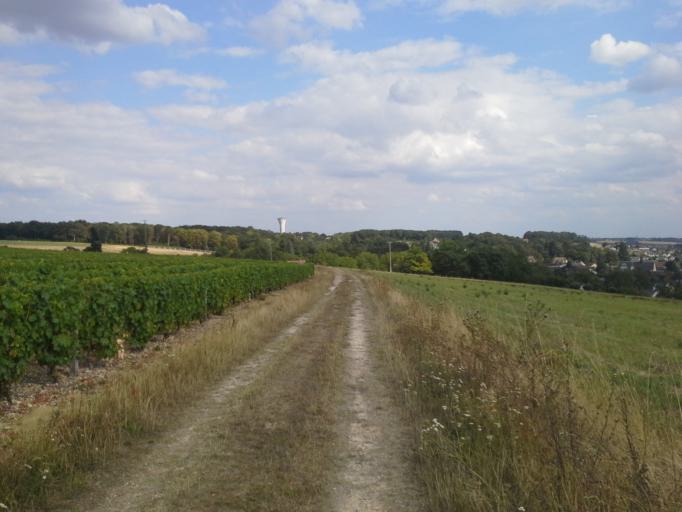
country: FR
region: Centre
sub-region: Departement du Loir-et-Cher
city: Villiers-sur-Loir
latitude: 47.8112
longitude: 0.9878
